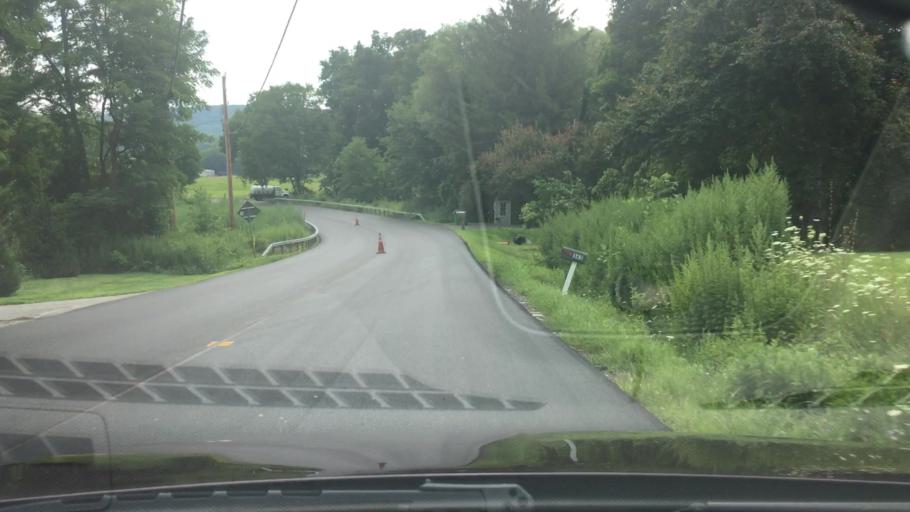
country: US
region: New York
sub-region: Dutchess County
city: Hillside Lake
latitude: 41.5783
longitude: -73.7396
